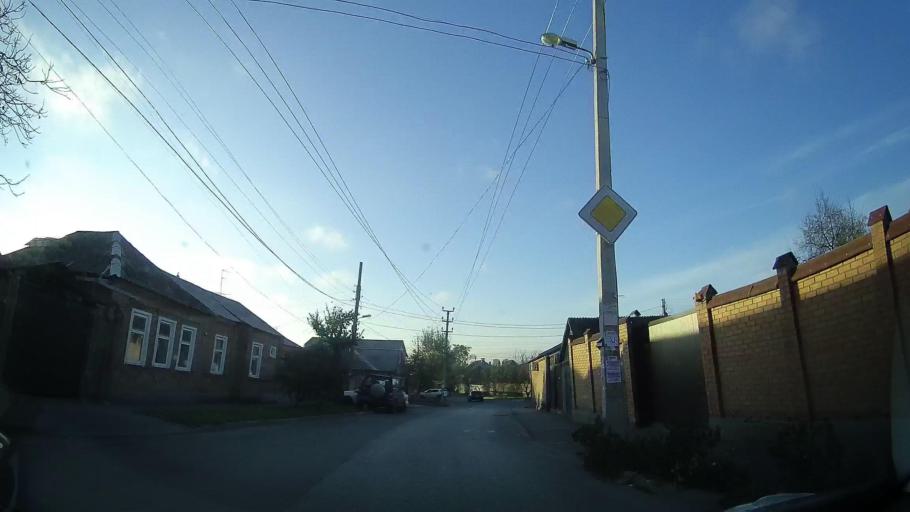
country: RU
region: Rostov
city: Severnyy
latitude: 47.2651
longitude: 39.6805
